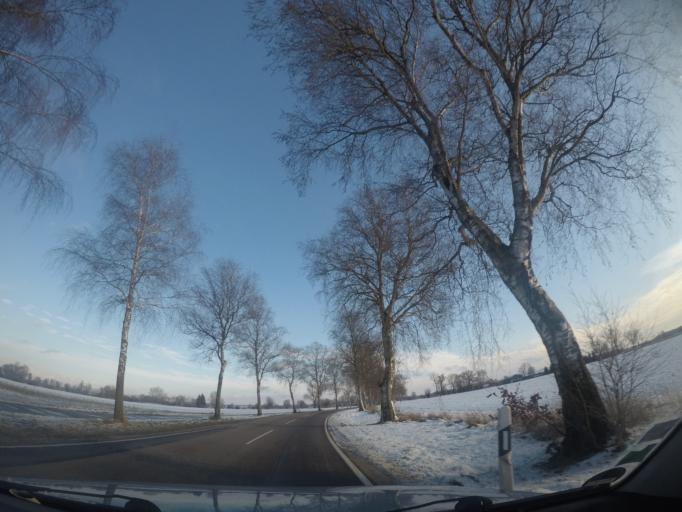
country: DE
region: Baden-Wuerttemberg
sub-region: Tuebingen Region
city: Ersingen
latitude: 48.2584
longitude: 9.8400
